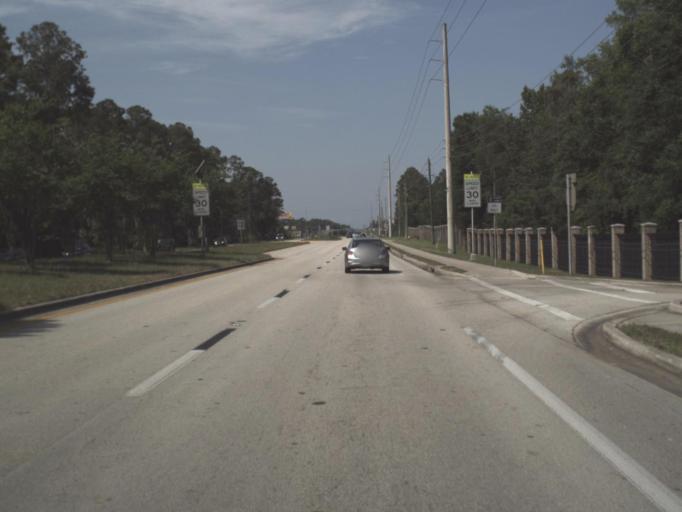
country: US
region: Florida
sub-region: Saint Johns County
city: Saint Augustine South
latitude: 29.8332
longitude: -81.3729
